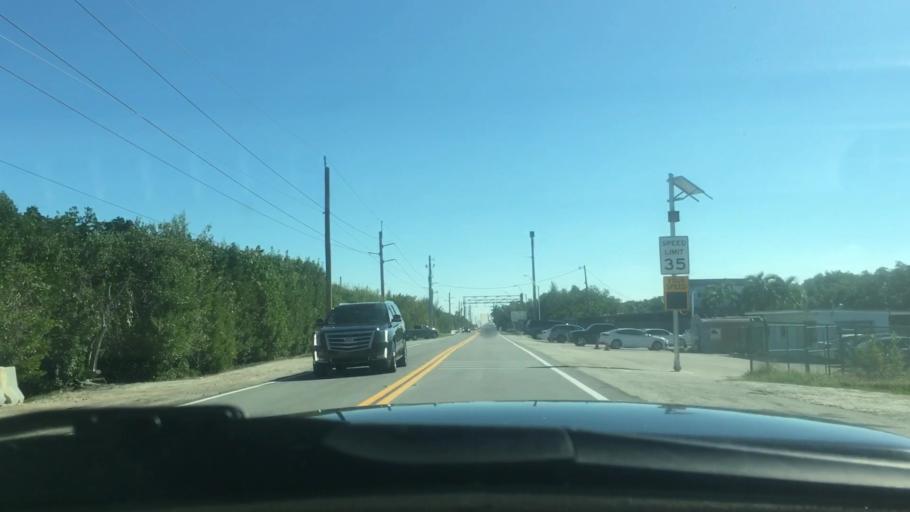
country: US
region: Florida
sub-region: Monroe County
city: North Key Largo
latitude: 25.2919
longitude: -80.3796
